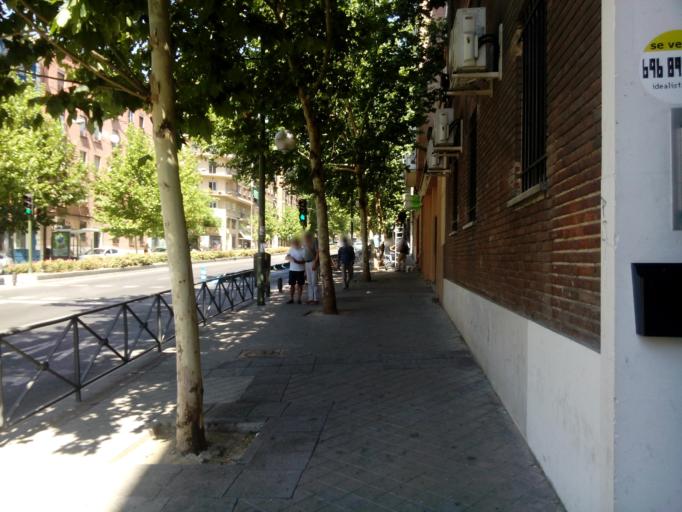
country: ES
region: Madrid
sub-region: Provincia de Madrid
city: Arganzuela
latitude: 40.3978
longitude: -3.7020
